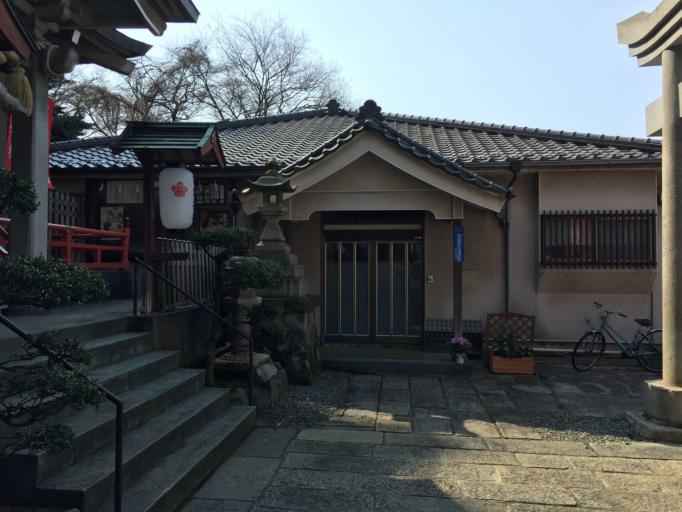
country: JP
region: Kanagawa
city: Yokohama
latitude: 35.4366
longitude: 139.6393
